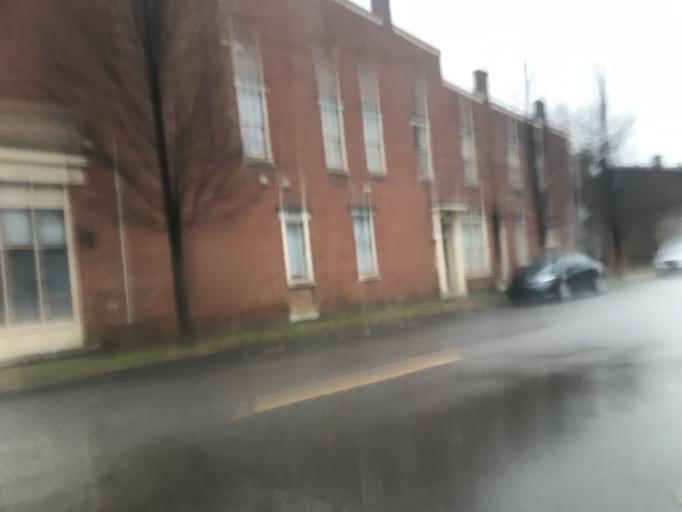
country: US
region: Kentucky
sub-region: Jefferson County
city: Louisville
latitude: 38.2480
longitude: -85.7390
